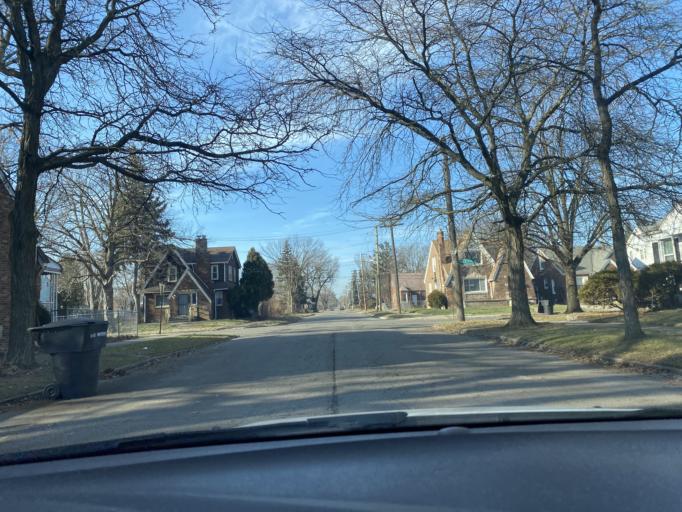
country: US
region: Michigan
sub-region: Wayne County
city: Harper Woods
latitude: 42.4107
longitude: -82.9499
